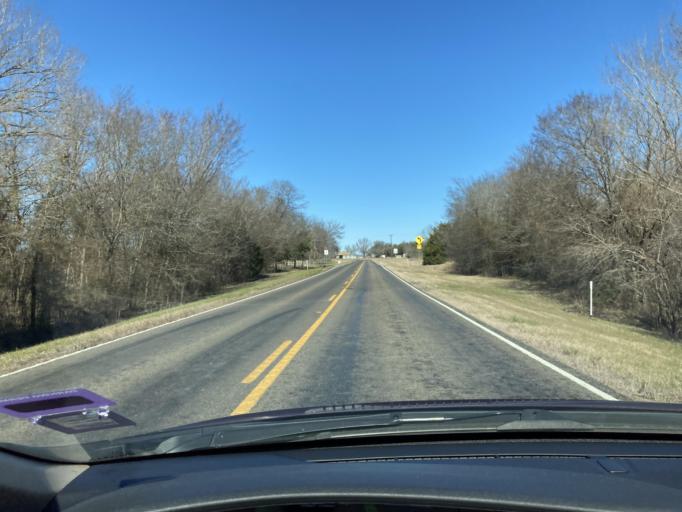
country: US
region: Texas
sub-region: Navarro County
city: Corsicana
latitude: 32.0585
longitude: -96.4986
